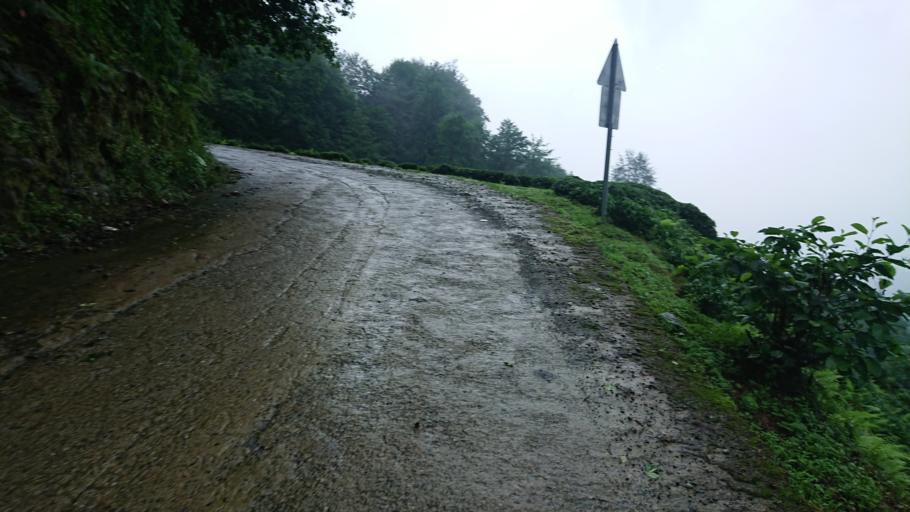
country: TR
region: Rize
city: Rize
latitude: 40.9765
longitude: 40.4959
